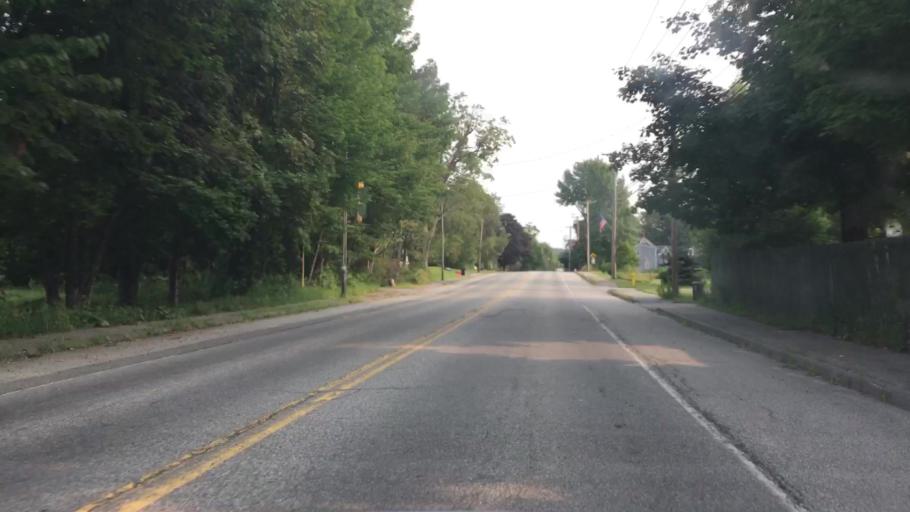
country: US
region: Maine
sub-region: Kennebec County
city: Gardiner
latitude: 44.2192
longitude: -69.7803
